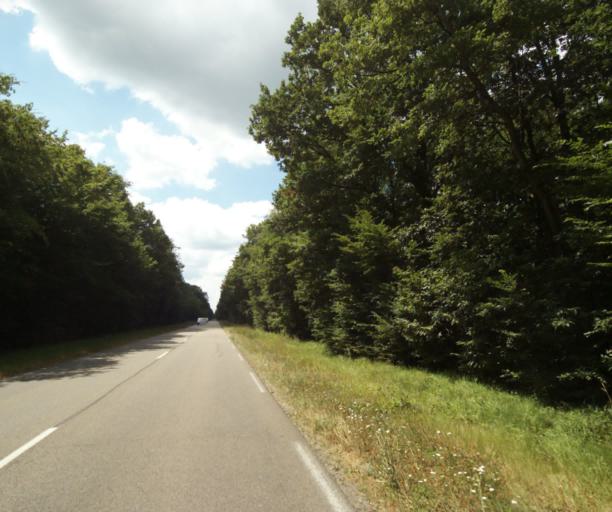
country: FR
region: Ile-de-France
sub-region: Departement de Seine-et-Marne
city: Thomery
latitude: 48.4203
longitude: 2.8027
